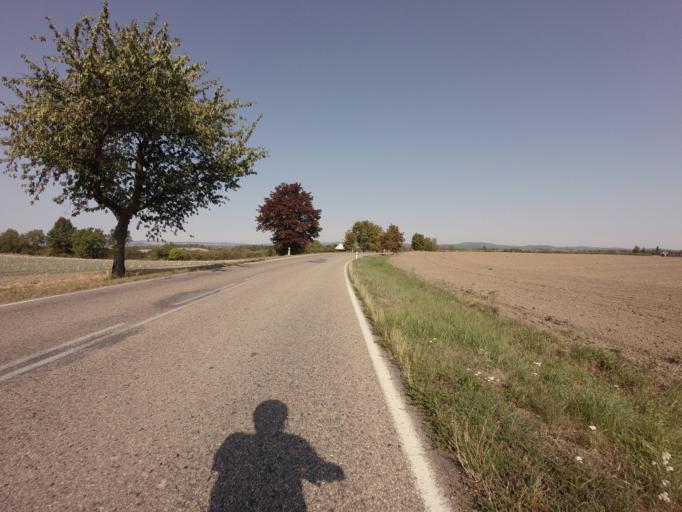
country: CZ
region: Central Bohemia
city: Porici nad Sazavou
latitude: 49.8097
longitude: 14.6471
